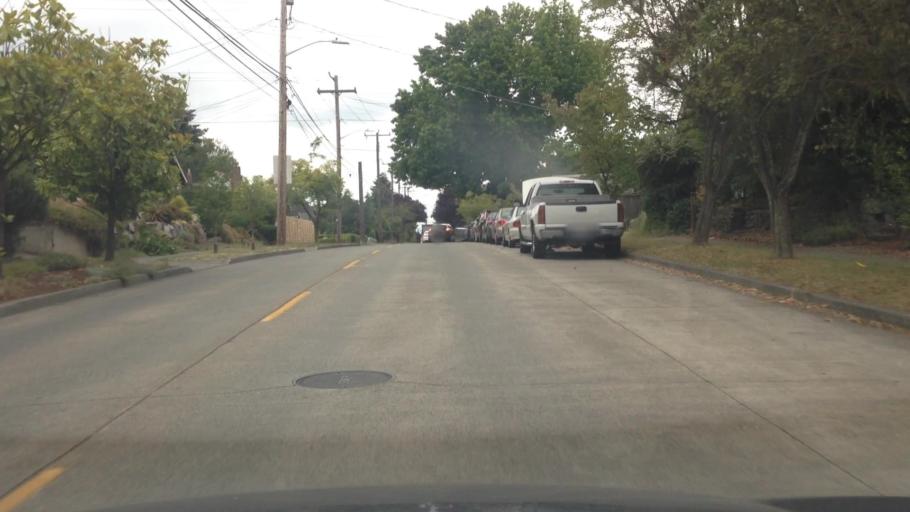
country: US
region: Washington
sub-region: King County
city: Shoreline
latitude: 47.6868
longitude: -122.3214
